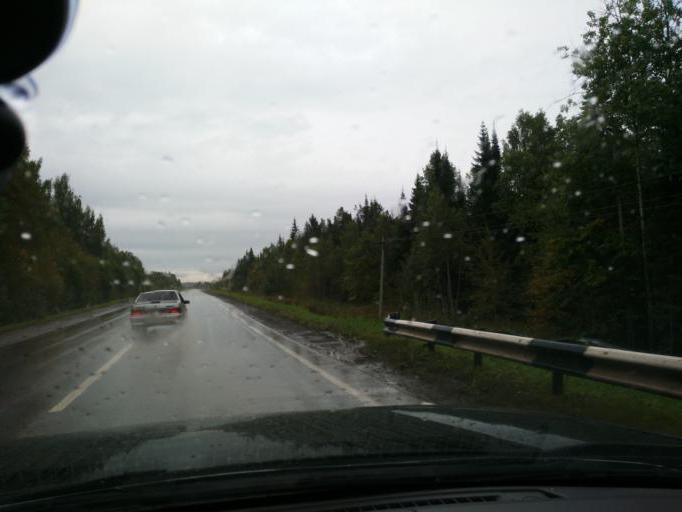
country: RU
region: Perm
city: Kultayevo
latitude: 57.8192
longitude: 55.8007
